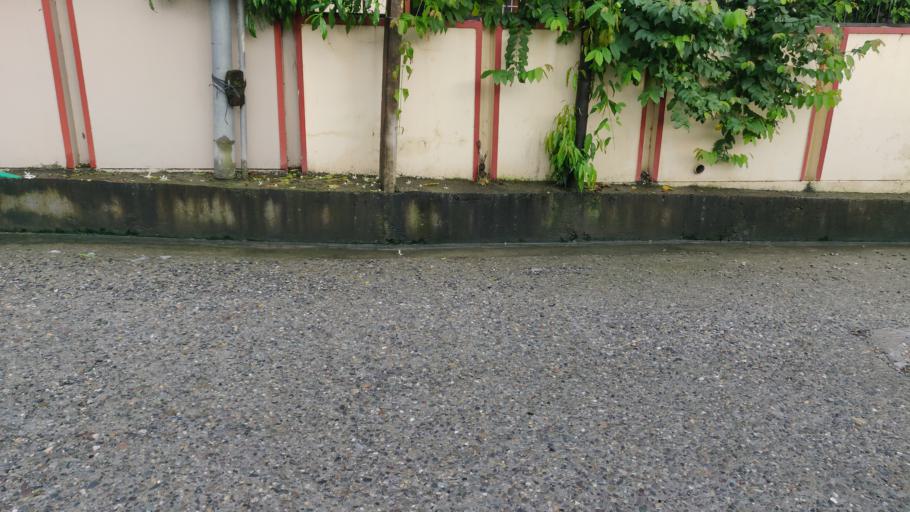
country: IN
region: Uttarakhand
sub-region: Dehradun
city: Dehradun
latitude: 30.3320
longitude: 78.0100
